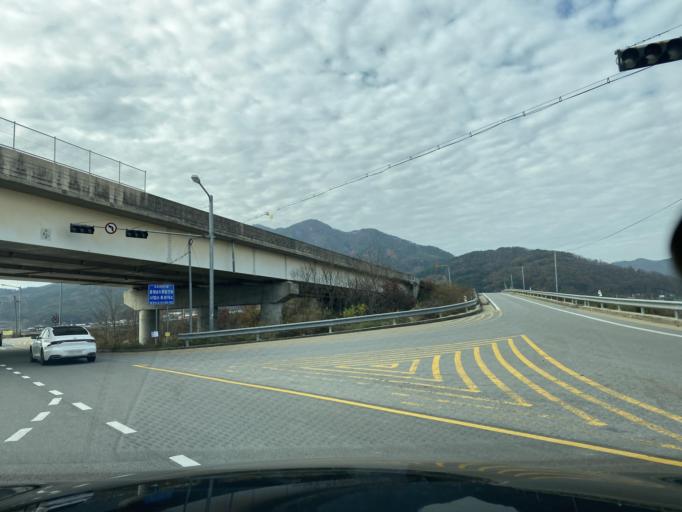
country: KR
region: Chungcheongnam-do
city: Hongsung
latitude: 36.6816
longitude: 126.6476
